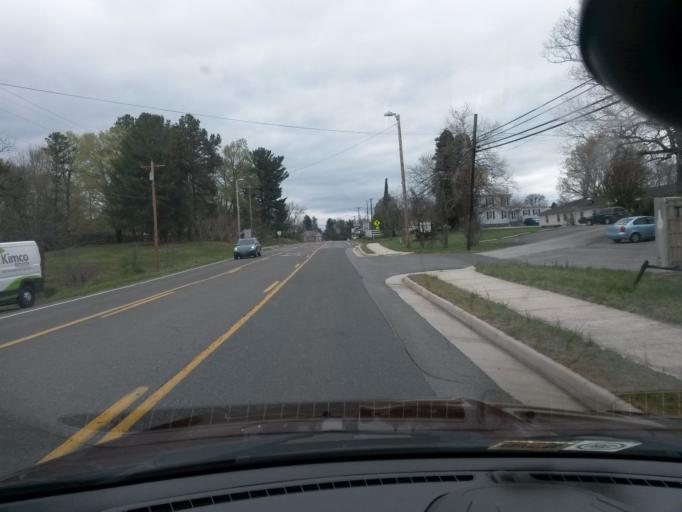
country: US
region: Virginia
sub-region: Amherst County
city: Amherst
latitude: 37.5783
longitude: -79.0574
